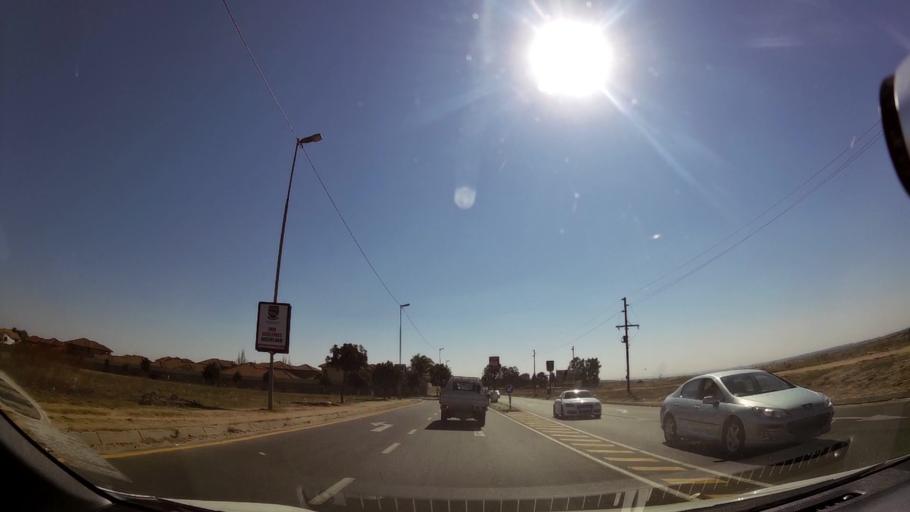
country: ZA
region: Gauteng
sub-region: City of Johannesburg Metropolitan Municipality
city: Midrand
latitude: -25.9660
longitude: 28.1020
